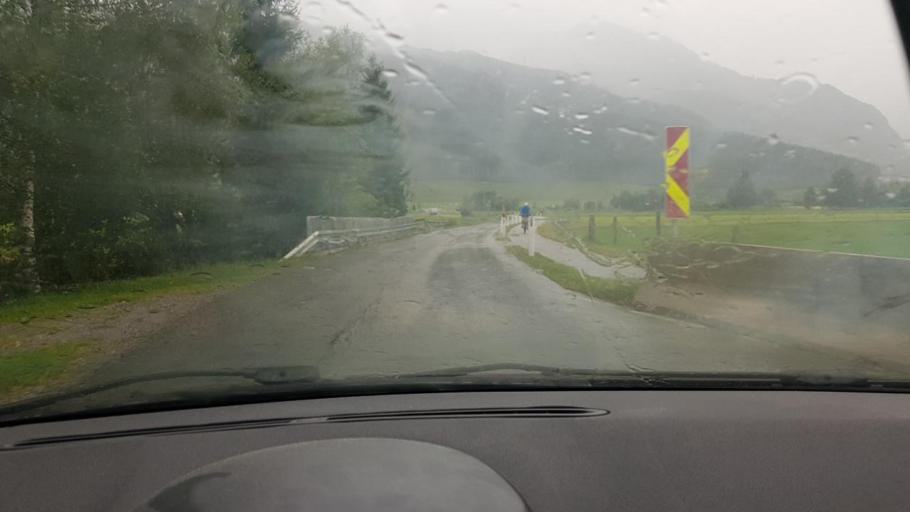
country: AT
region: Salzburg
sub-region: Politischer Bezirk Zell am See
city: Kaprun
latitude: 47.2863
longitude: 12.7846
